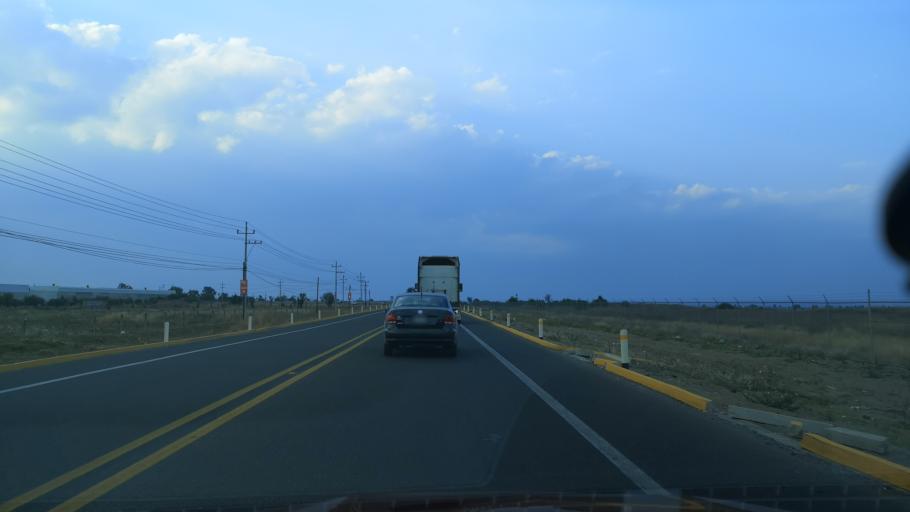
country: MX
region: Puebla
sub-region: Juan C. Bonilla
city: Santa Maria Zacatepec
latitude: 19.1488
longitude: -98.3741
